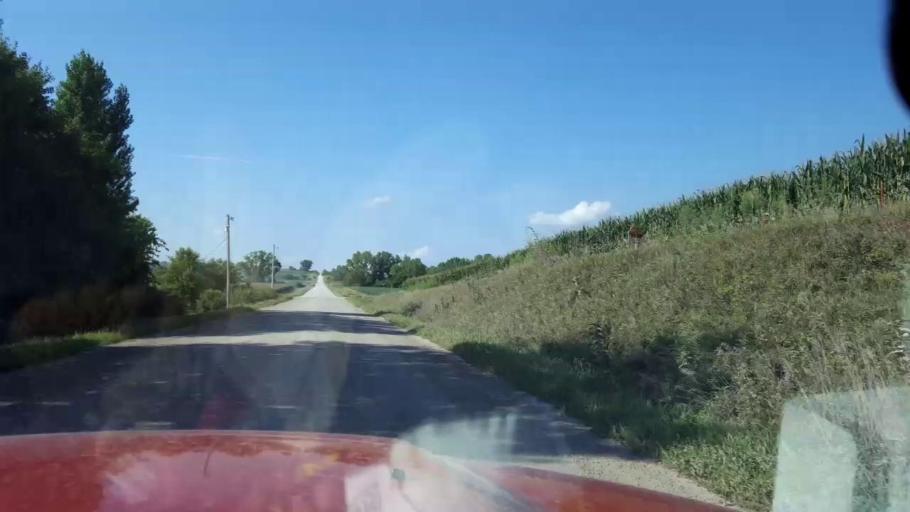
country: US
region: Iowa
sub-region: Pottawattamie County
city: Oakland
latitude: 41.2446
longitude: -95.5371
